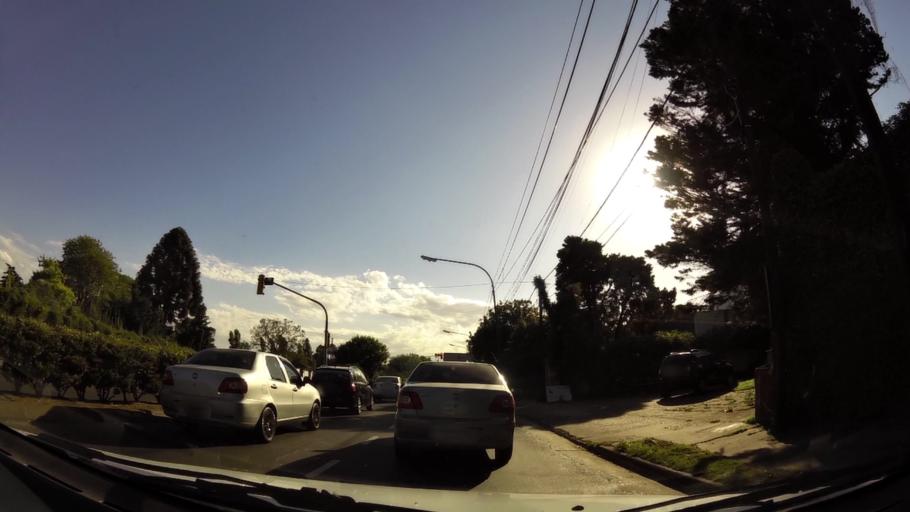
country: AR
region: Buenos Aires
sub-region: Partido de San Isidro
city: San Isidro
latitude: -34.4898
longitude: -58.5425
